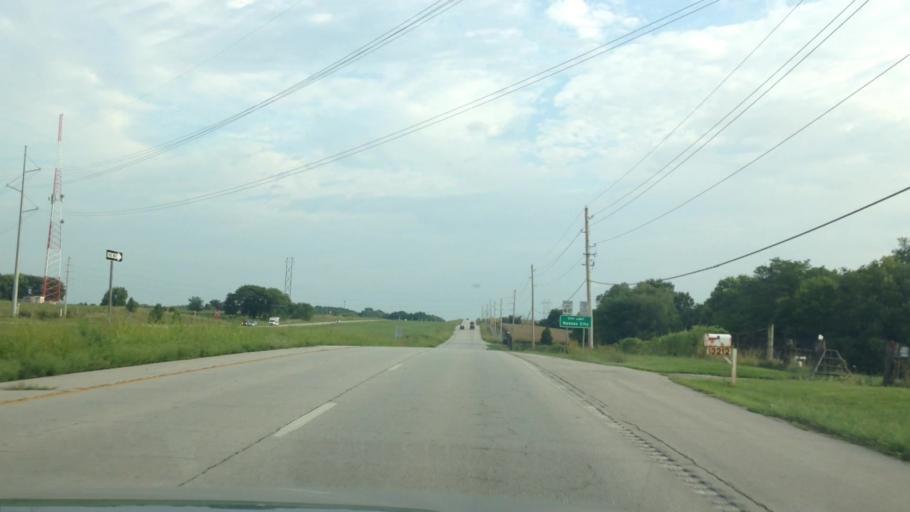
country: US
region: Missouri
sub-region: Clay County
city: Smithville
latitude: 39.3338
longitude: -94.5844
